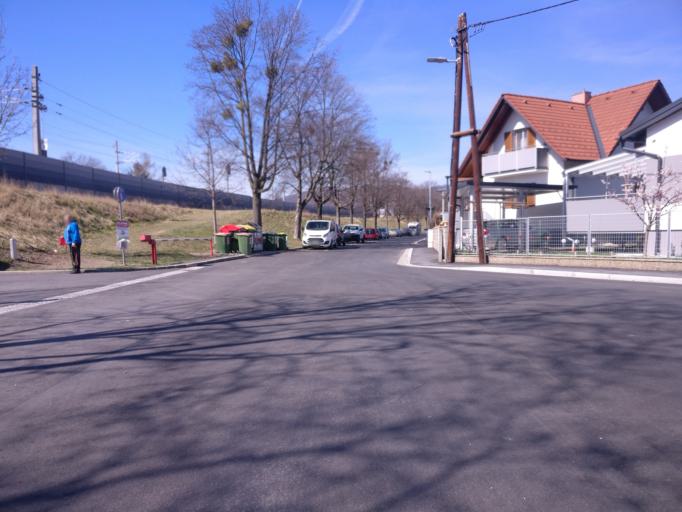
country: AT
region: Styria
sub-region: Graz Stadt
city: Wetzelsdorf
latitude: 47.0562
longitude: 15.4229
